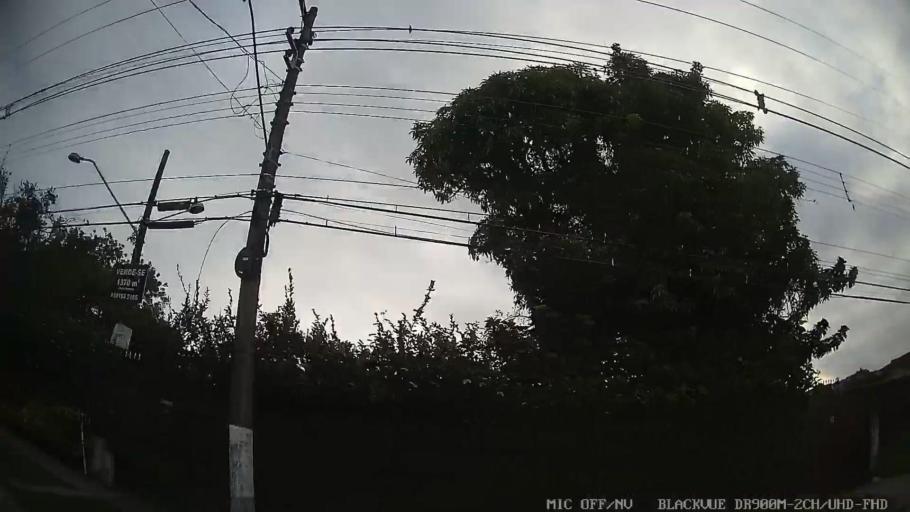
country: BR
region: Sao Paulo
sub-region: Guaruja
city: Guaruja
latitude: -23.9767
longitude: -46.2098
